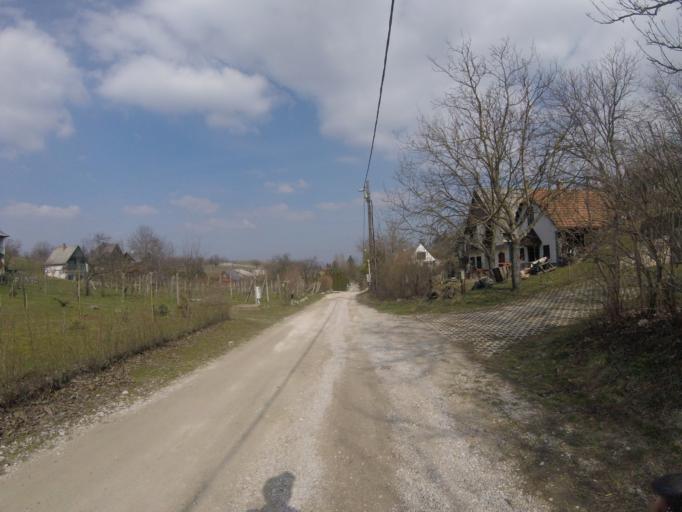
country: HU
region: Komarom-Esztergom
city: Nyergesujfalu
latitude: 47.7419
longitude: 18.5525
